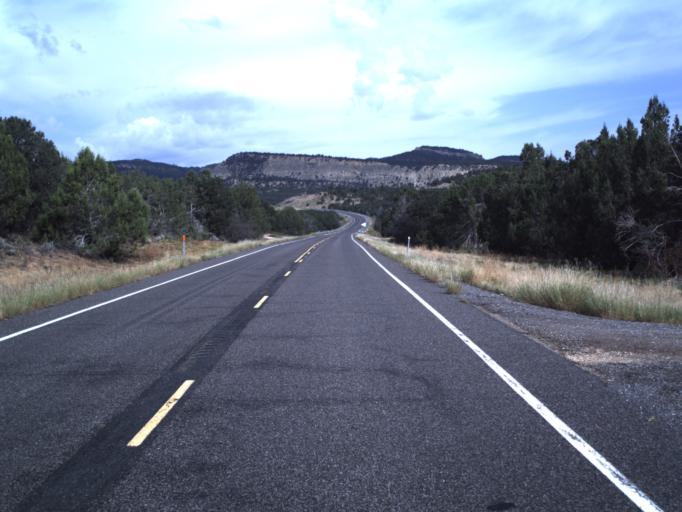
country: US
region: Utah
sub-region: Kane County
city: Kanab
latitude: 37.2531
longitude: -112.7626
